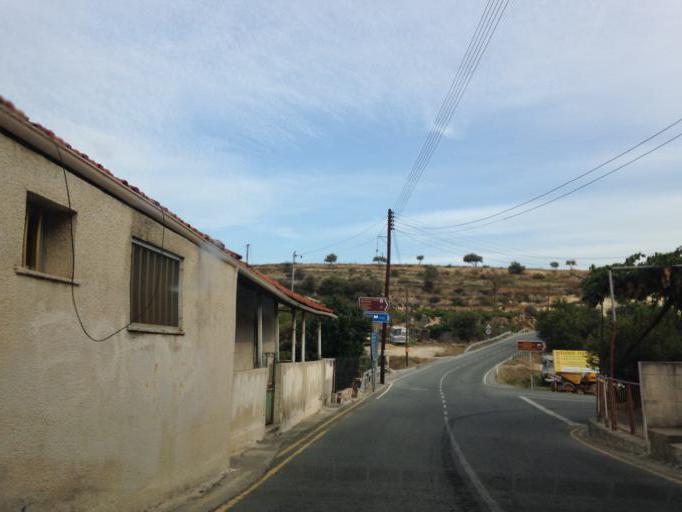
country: CY
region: Limassol
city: Pachna
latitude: 34.7794
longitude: 32.7968
